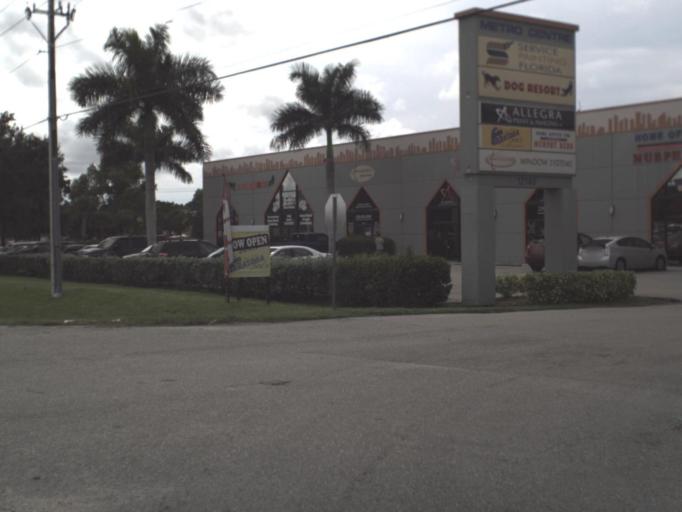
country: US
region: Florida
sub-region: Lee County
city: Villas
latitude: 26.5662
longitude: -81.8531
